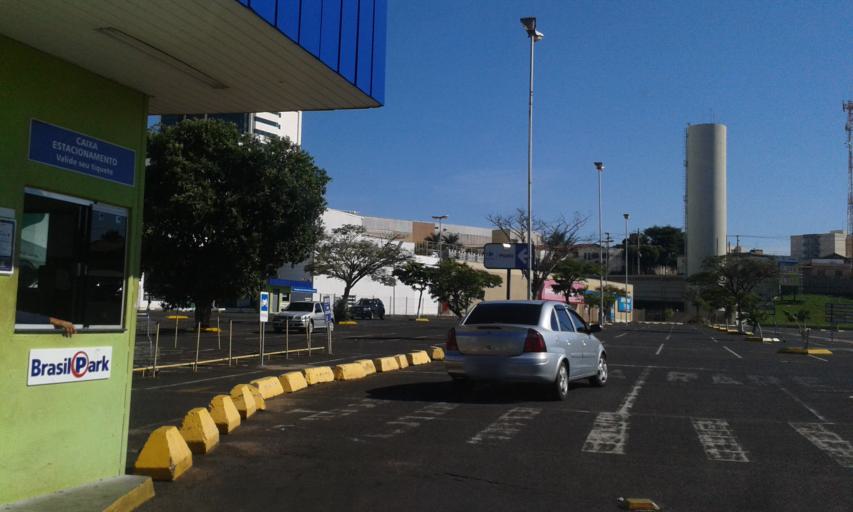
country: BR
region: Minas Gerais
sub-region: Uberlandia
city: Uberlandia
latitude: -18.9117
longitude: -48.2590
